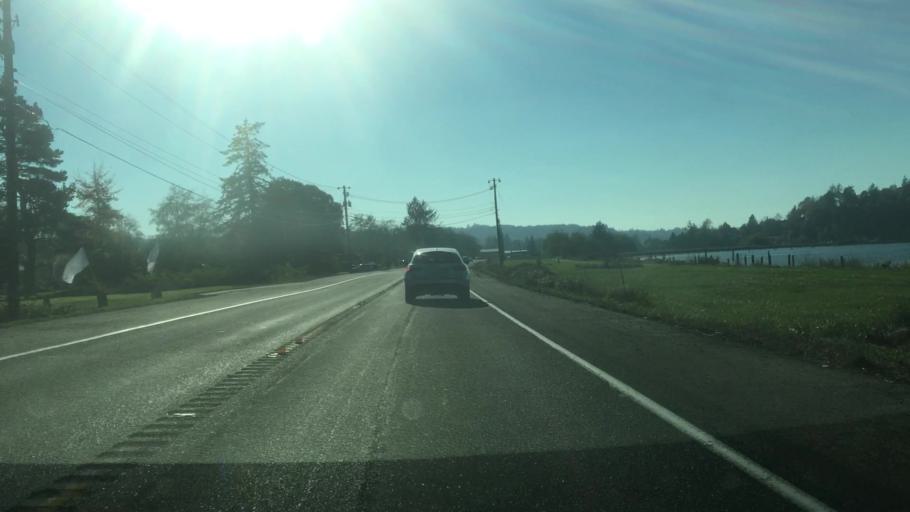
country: US
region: Washington
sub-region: Pacific County
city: Raymond
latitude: 46.6759
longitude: -123.7644
